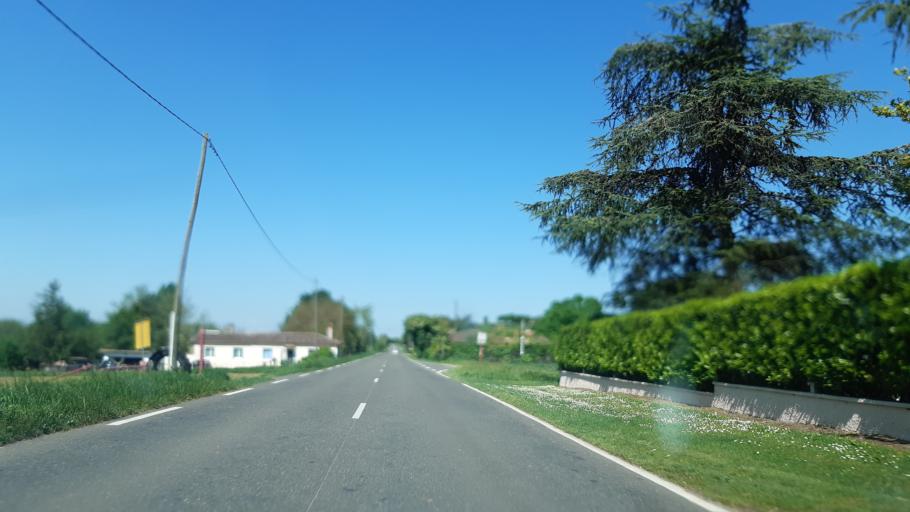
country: FR
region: Midi-Pyrenees
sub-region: Departement du Gers
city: Pujaudran
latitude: 43.5848
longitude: 1.0488
